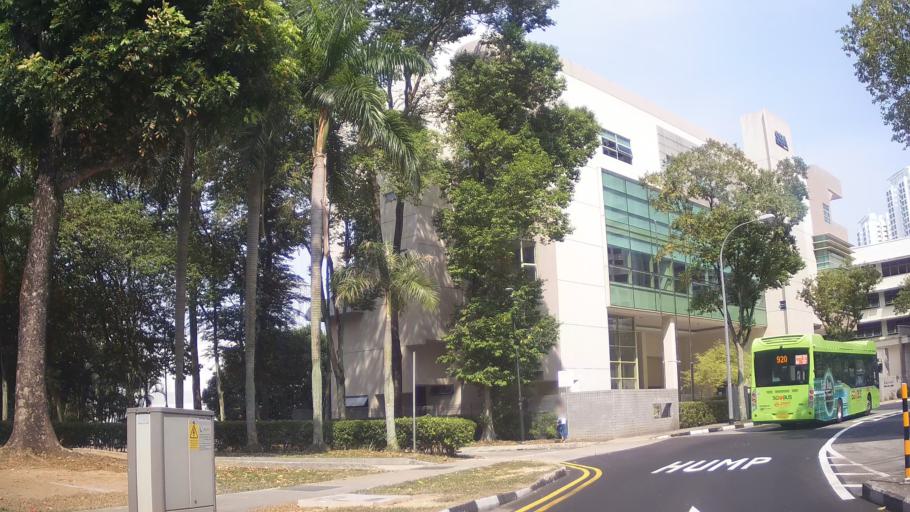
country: MY
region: Johor
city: Johor Bahru
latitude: 1.3821
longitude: 103.7616
